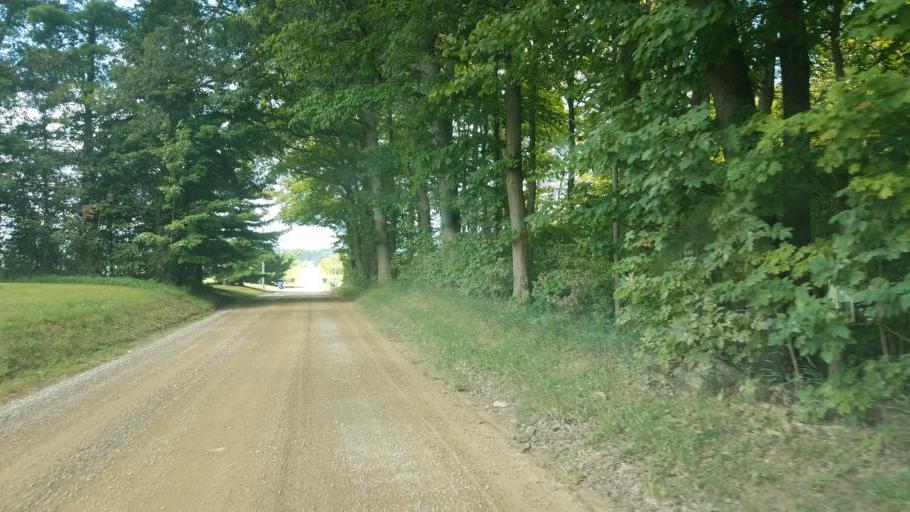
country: US
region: Ohio
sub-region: Licking County
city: Utica
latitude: 40.2525
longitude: -82.4037
